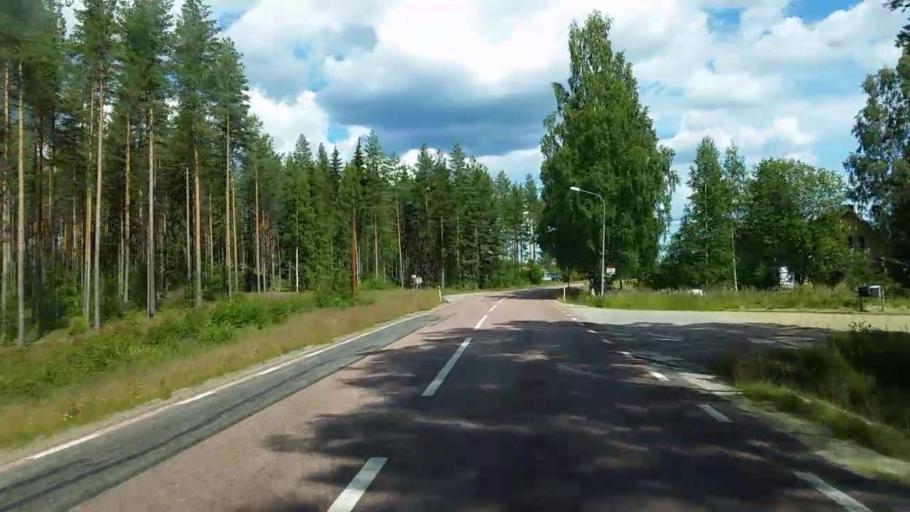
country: SE
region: Gaevleborg
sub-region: Ovanakers Kommun
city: Edsbyn
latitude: 61.3581
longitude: 15.6989
